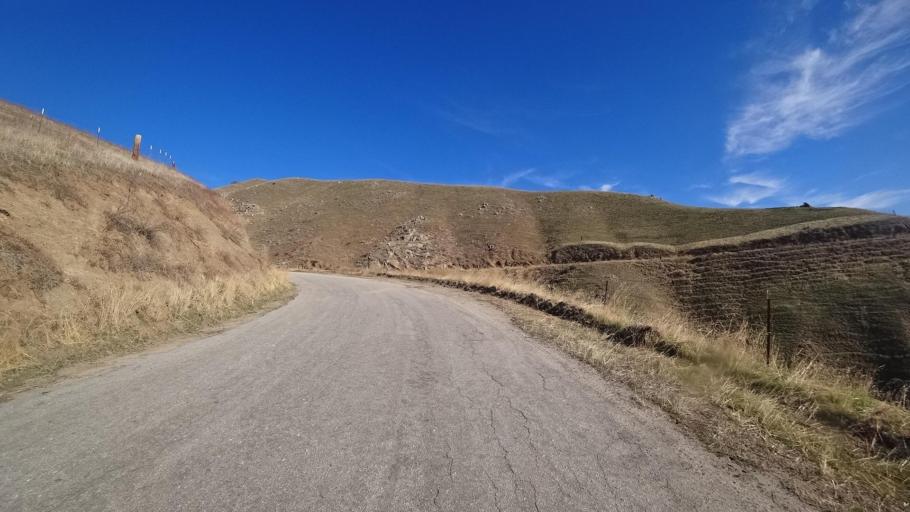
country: US
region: California
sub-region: Kern County
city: Arvin
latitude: 35.4250
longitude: -118.7328
